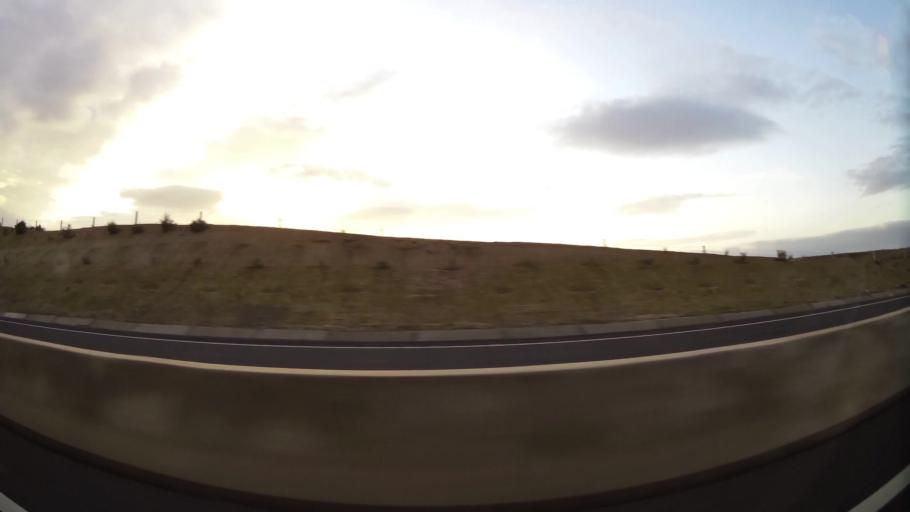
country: MA
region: Oriental
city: Taourirt
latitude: 34.4967
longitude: -2.9670
